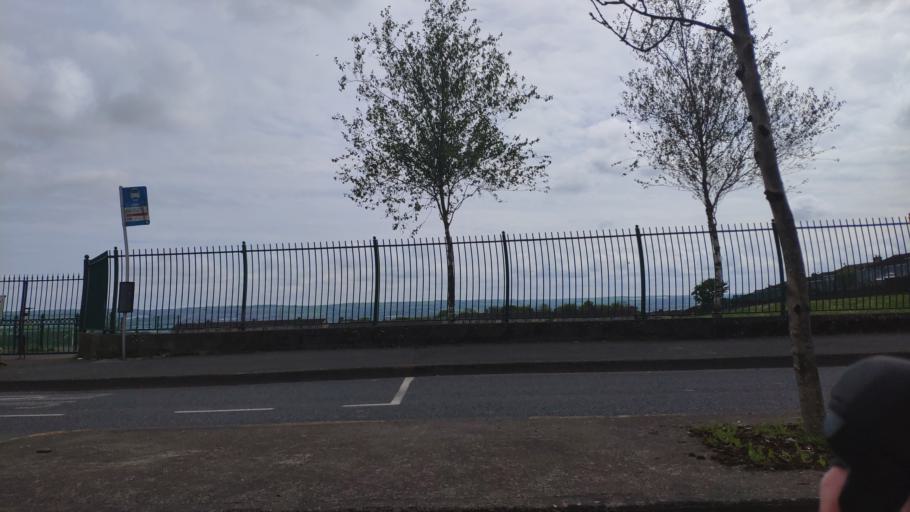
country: IE
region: Munster
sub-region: County Cork
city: Cork
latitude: 51.9080
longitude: -8.5067
